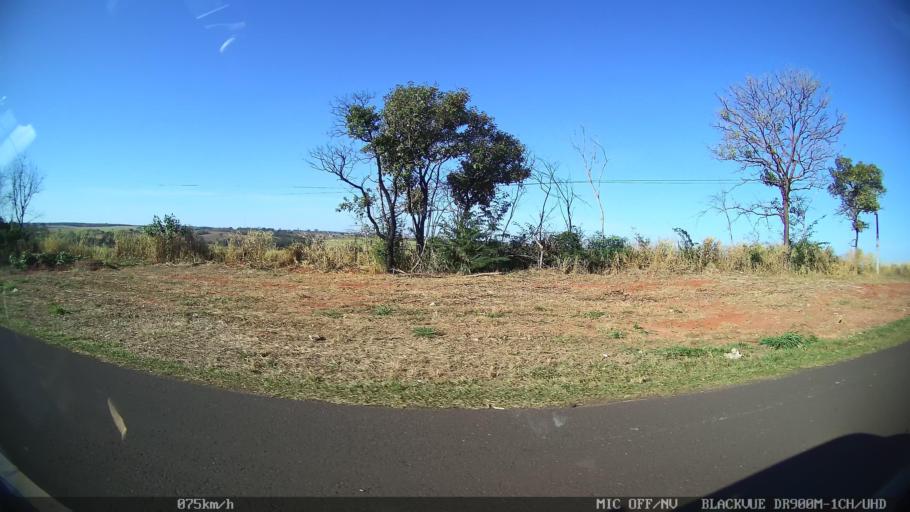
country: BR
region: Sao Paulo
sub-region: Olimpia
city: Olimpia
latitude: -20.6991
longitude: -48.9144
